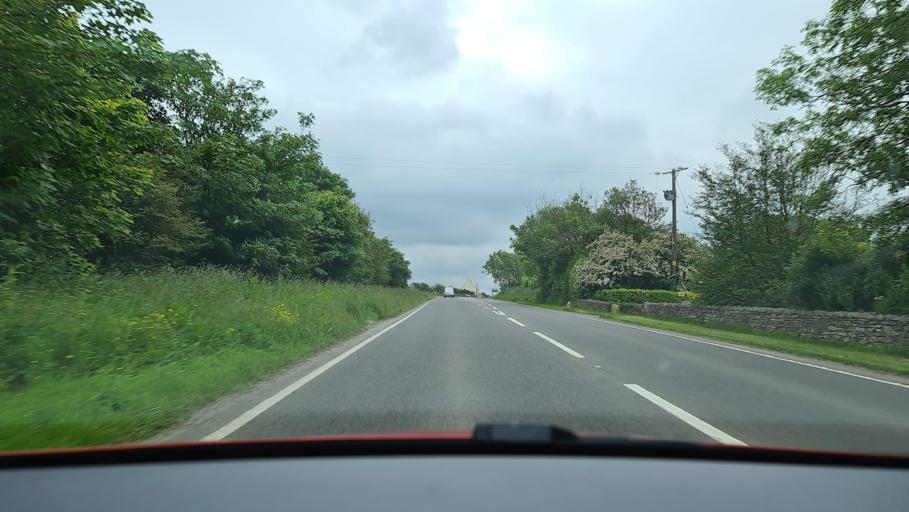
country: GB
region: England
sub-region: Cornwall
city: Camelford
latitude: 50.6530
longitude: -4.6352
